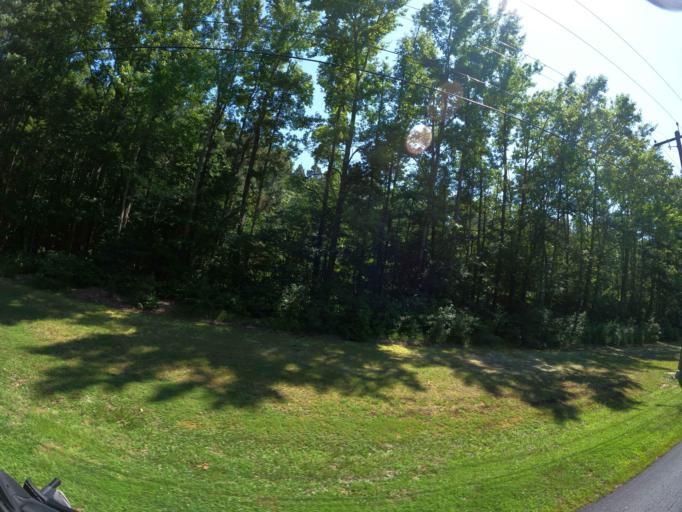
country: US
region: Maryland
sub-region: Worcester County
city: Ocean Pines
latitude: 38.4512
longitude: -75.1448
